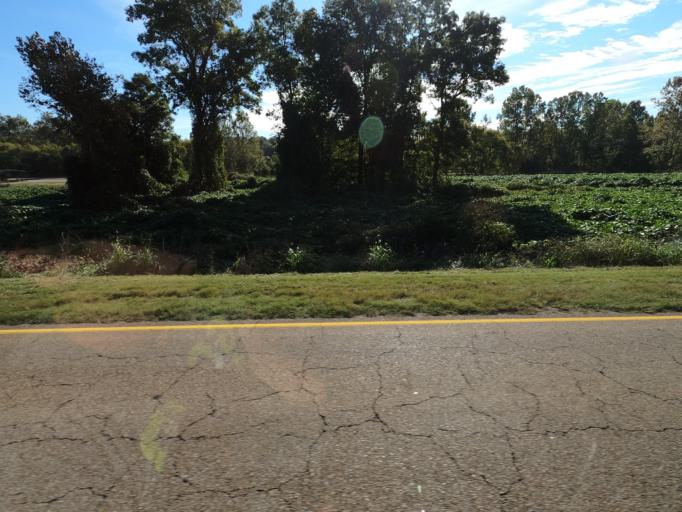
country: US
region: Tennessee
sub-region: Tipton County
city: Brighton
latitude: 35.5121
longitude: -89.7096
